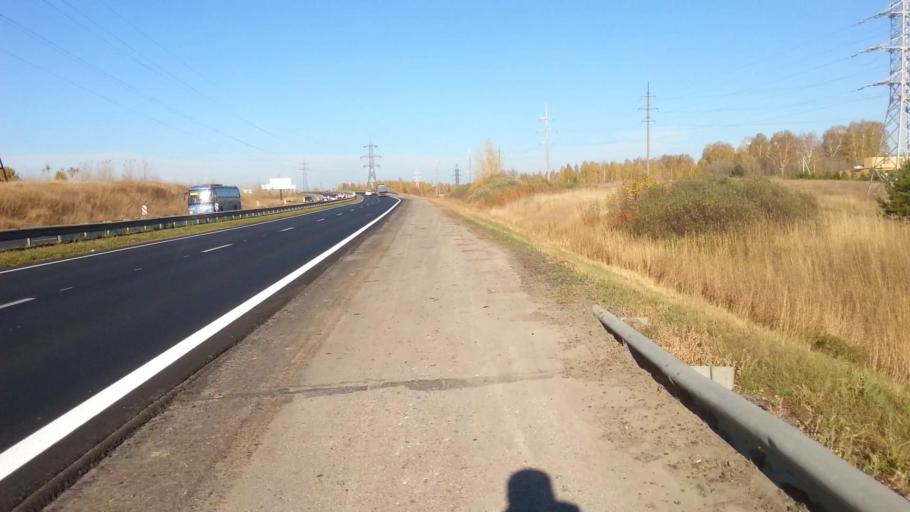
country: RU
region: Altai Krai
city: Sannikovo
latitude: 53.3458
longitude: 83.9437
